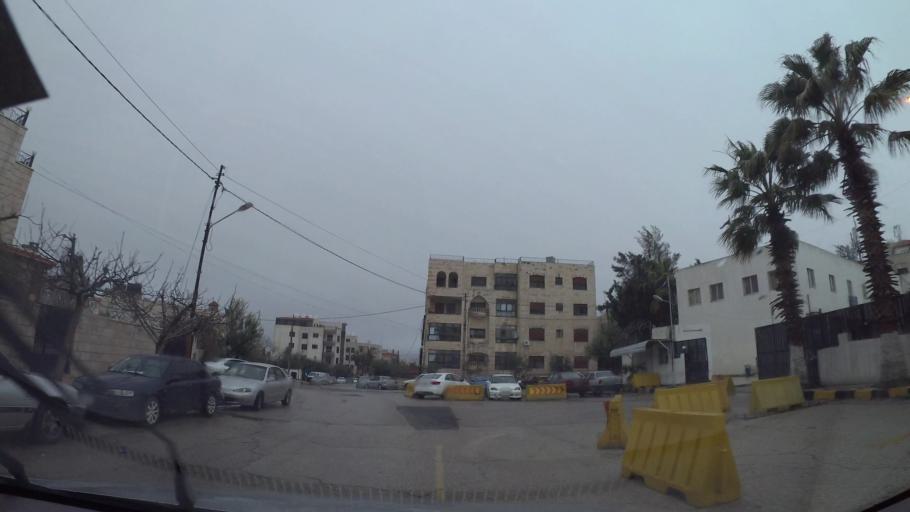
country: JO
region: Amman
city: Al Jubayhah
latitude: 32.0299
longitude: 35.8527
